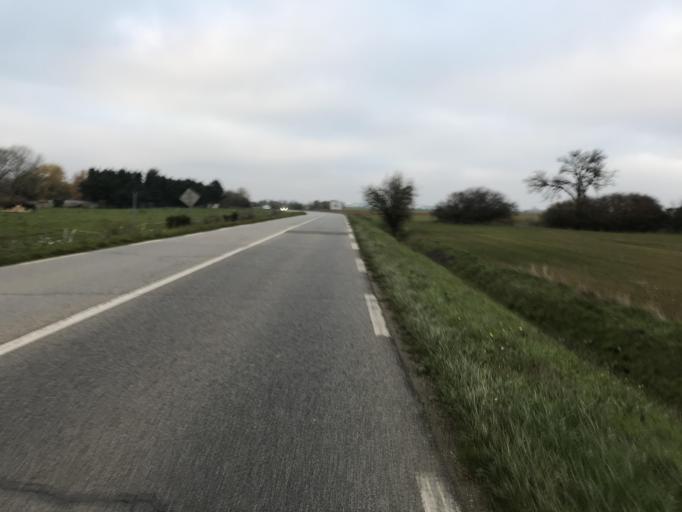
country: FR
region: Ile-de-France
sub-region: Departement des Yvelines
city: Chateaufort
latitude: 48.7366
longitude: 2.0971
